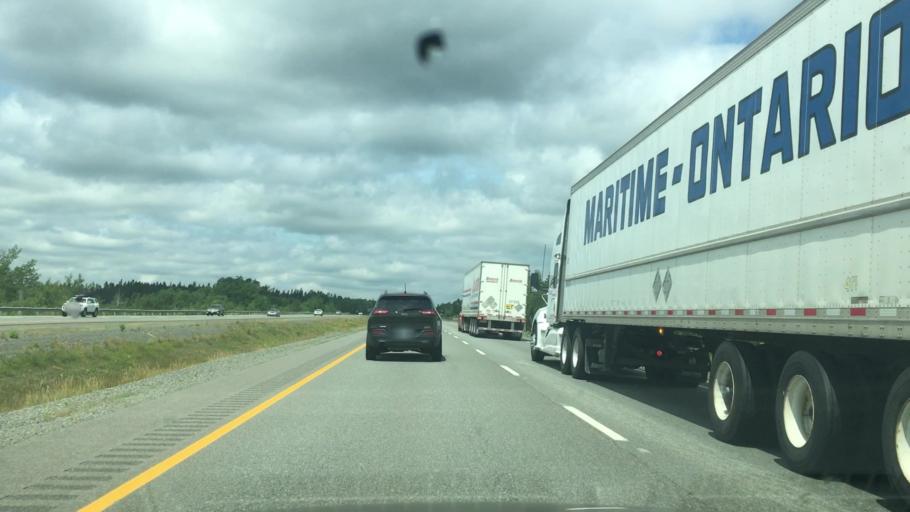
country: CA
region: Nova Scotia
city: Springhill
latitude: 45.7085
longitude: -64.0359
